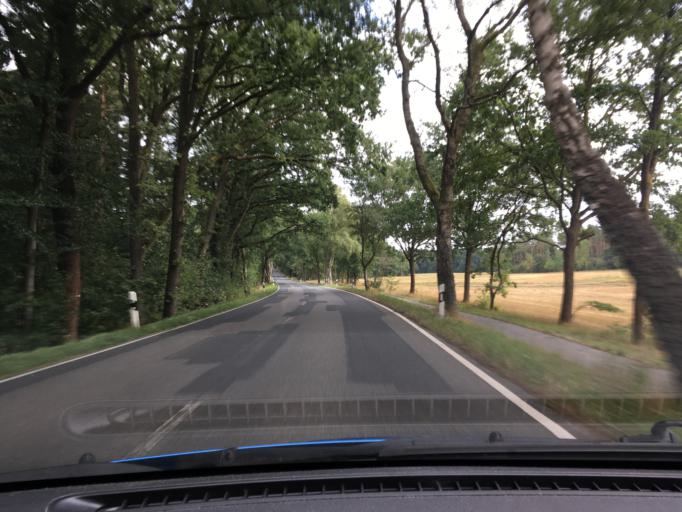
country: DE
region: Lower Saxony
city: Undeloh
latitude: 53.2016
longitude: 9.9647
